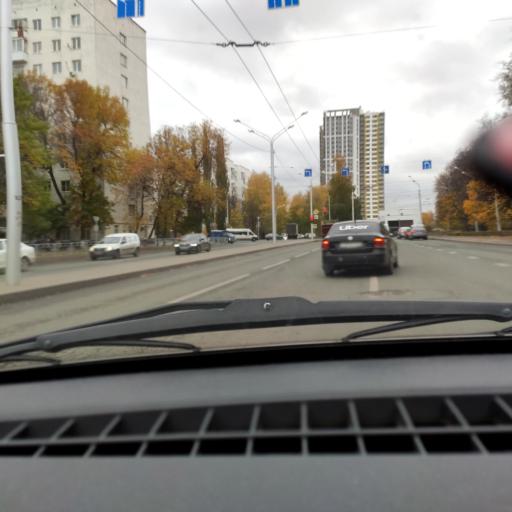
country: RU
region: Bashkortostan
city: Ufa
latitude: 54.7634
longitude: 56.0045
